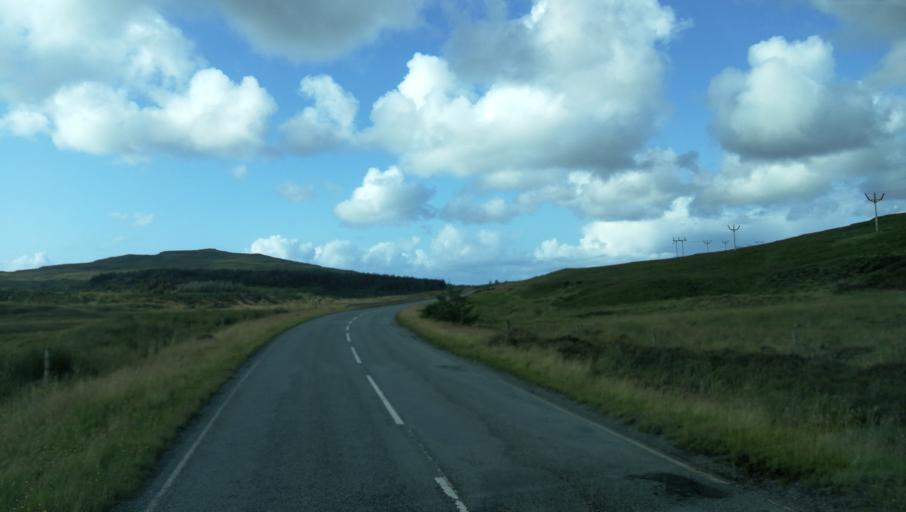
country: GB
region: Scotland
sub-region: Highland
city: Isle of Skye
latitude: 57.4485
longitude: -6.5432
